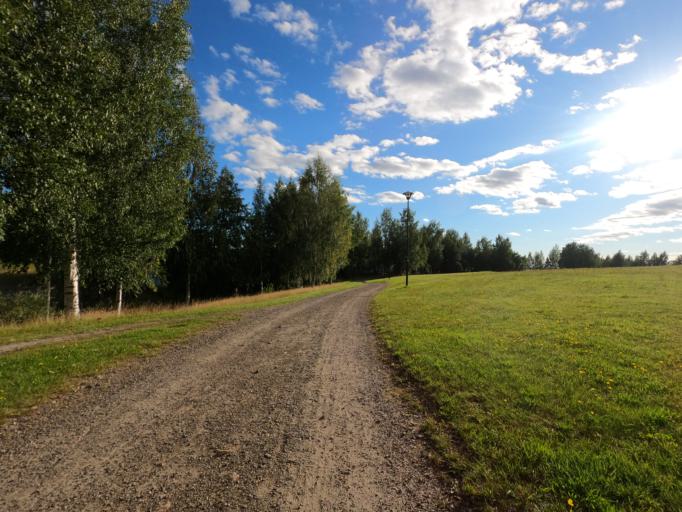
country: FI
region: North Karelia
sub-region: Joensuu
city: Joensuu
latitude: 62.5949
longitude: 29.7361
